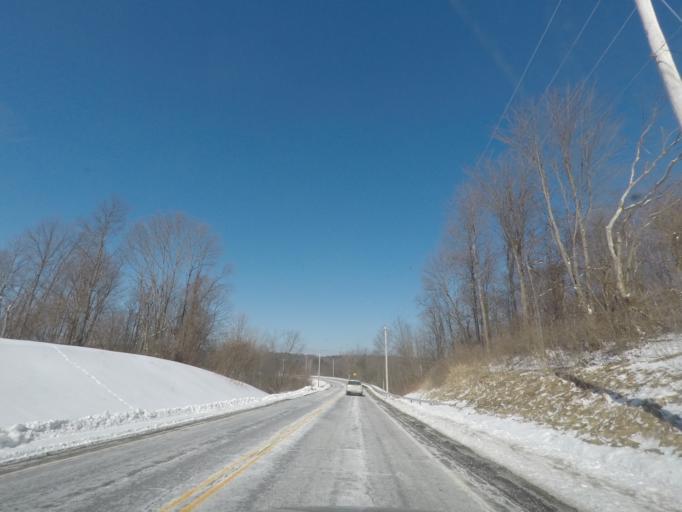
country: US
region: New York
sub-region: Saratoga County
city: Ballston Spa
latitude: 42.9938
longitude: -73.8003
